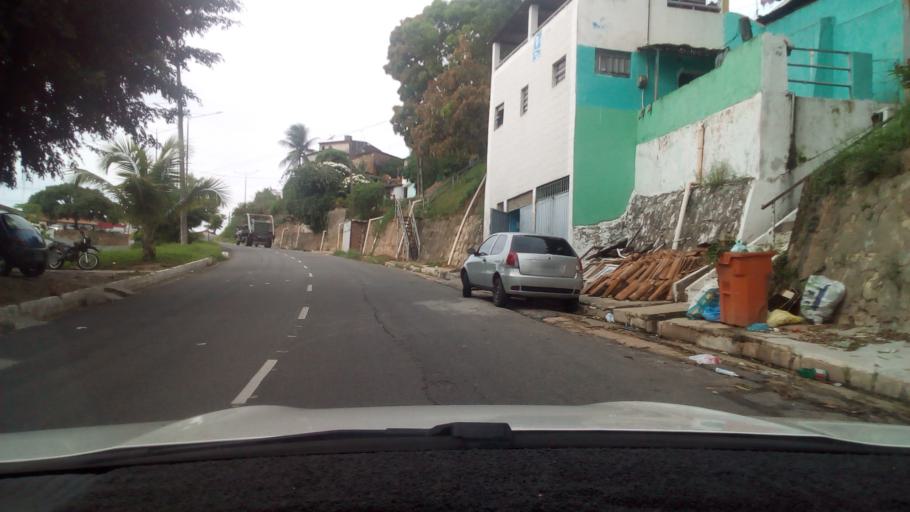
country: BR
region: Paraiba
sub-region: Joao Pessoa
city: Joao Pessoa
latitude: -7.1119
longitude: -34.8827
